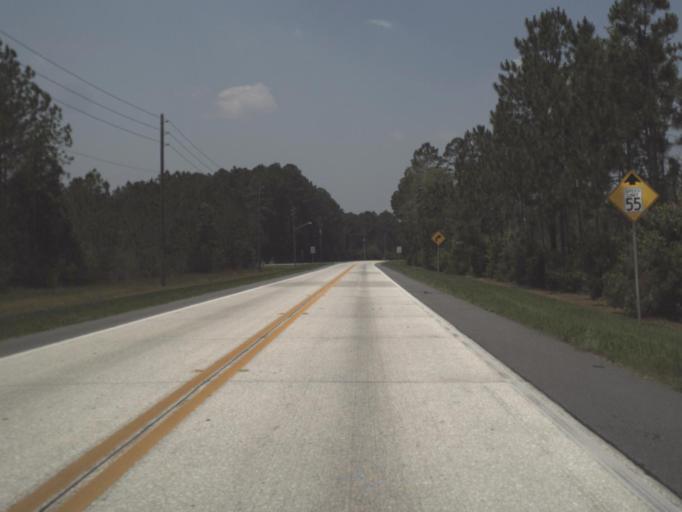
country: US
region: Florida
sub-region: Duval County
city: Baldwin
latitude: 30.2027
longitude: -82.0011
